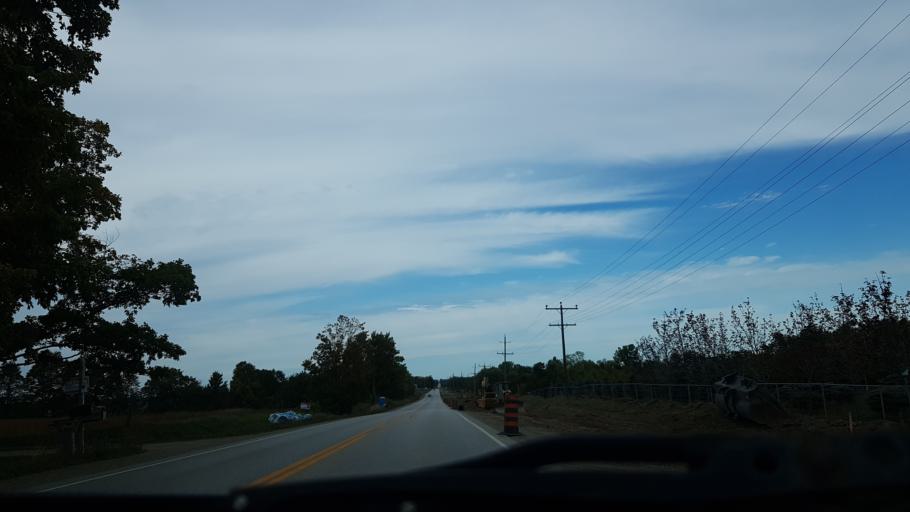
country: CA
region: Ontario
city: Wasaga Beach
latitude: 44.3812
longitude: -80.0879
